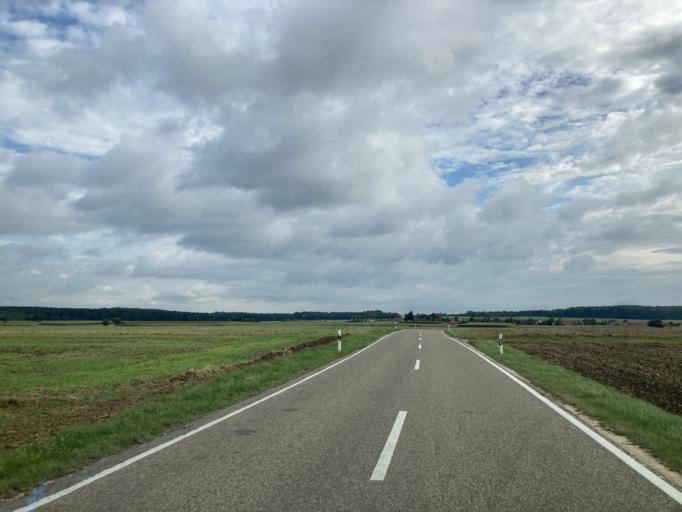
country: DE
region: Bavaria
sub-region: Swabia
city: Bachhagel
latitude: 48.6215
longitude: 10.3107
